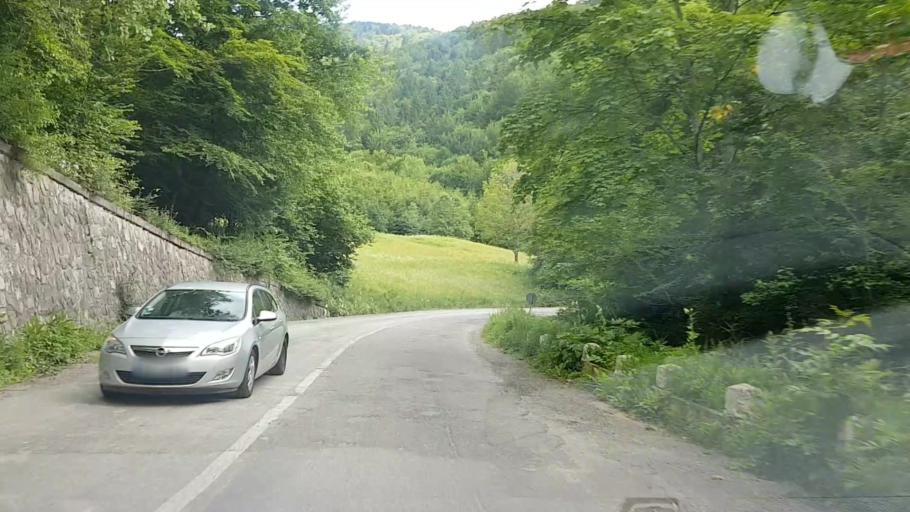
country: RO
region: Neamt
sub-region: Comuna Pangarati
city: Pangarati
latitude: 46.9359
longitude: 26.1267
